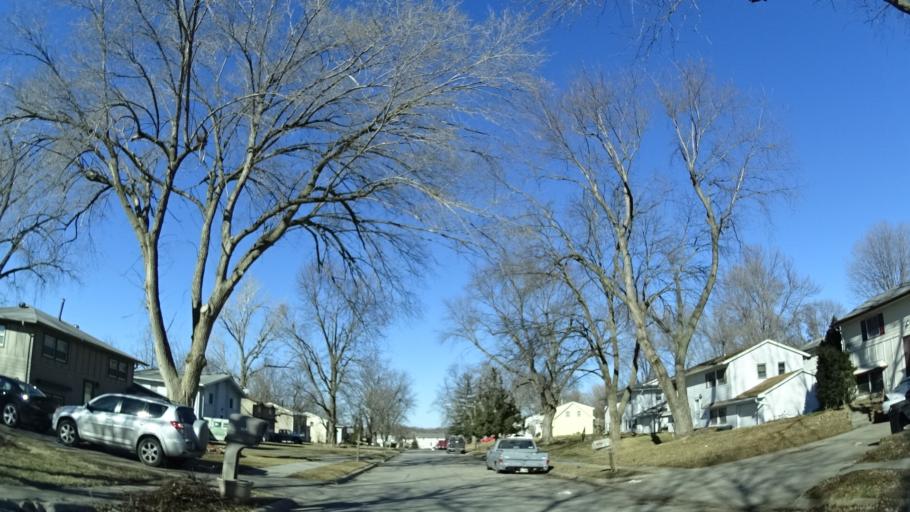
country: US
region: Nebraska
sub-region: Sarpy County
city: Offutt Air Force Base
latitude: 41.1451
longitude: -95.9182
